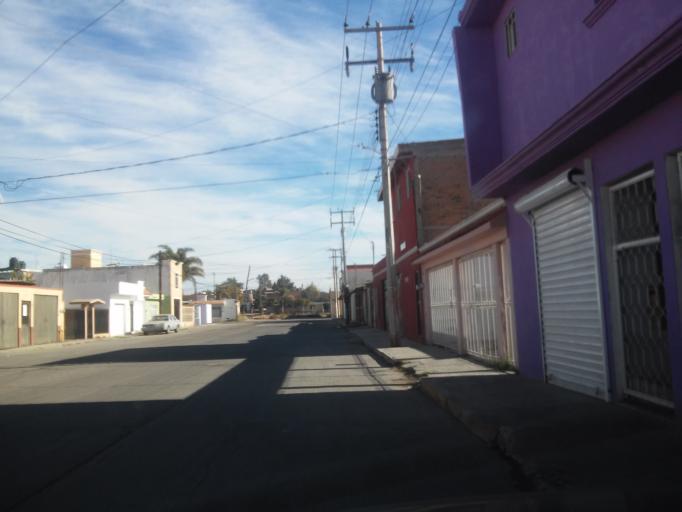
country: MX
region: Durango
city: Victoria de Durango
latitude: 24.0426
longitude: -104.6526
